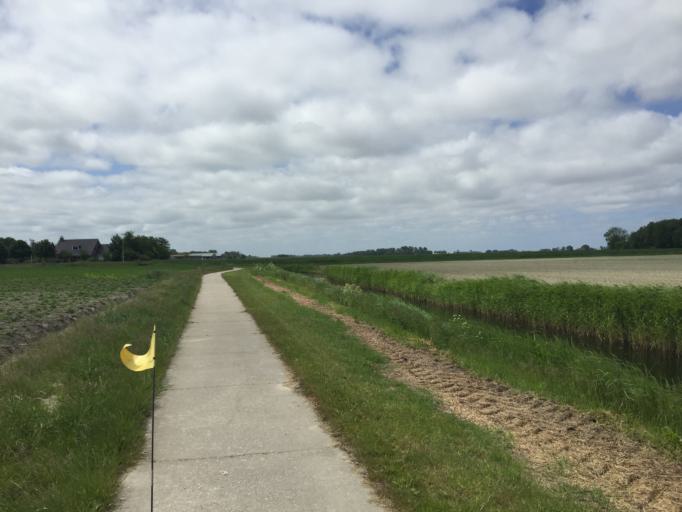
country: NL
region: Friesland
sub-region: Gemeente Dongeradeel
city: Anjum
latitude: 53.3845
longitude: 6.0585
